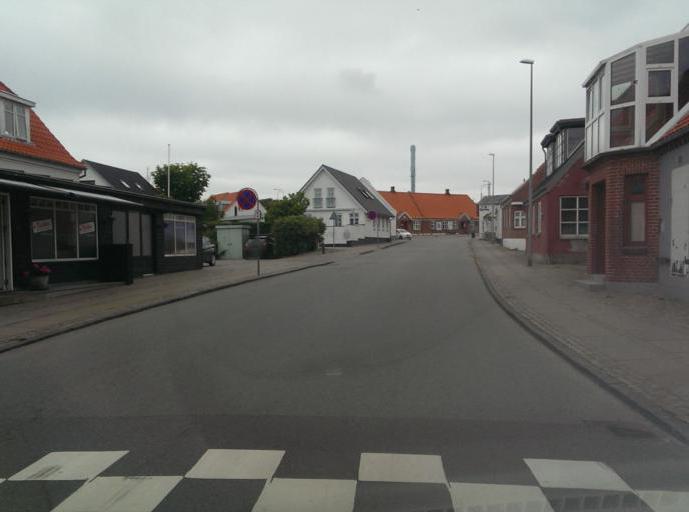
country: DK
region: South Denmark
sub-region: Fano Kommune
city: Nordby
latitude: 55.5231
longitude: 8.3543
